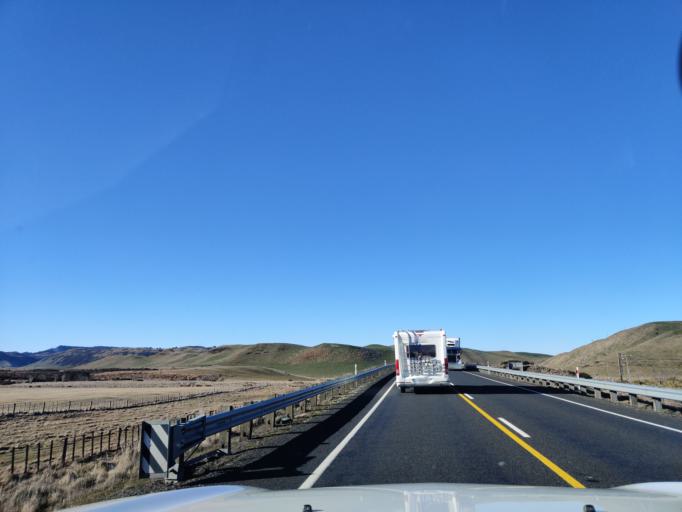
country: NZ
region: Manawatu-Wanganui
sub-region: Ruapehu District
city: Waiouru
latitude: -39.4975
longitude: 175.6736
